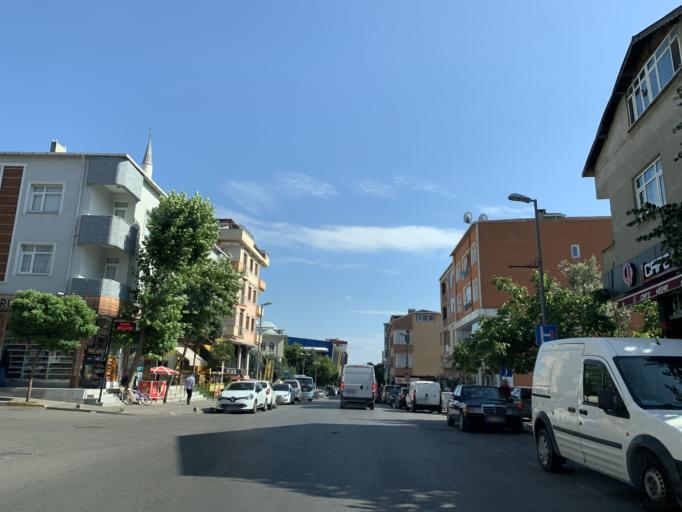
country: TR
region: Istanbul
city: Pendik
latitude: 40.8825
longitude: 29.2725
